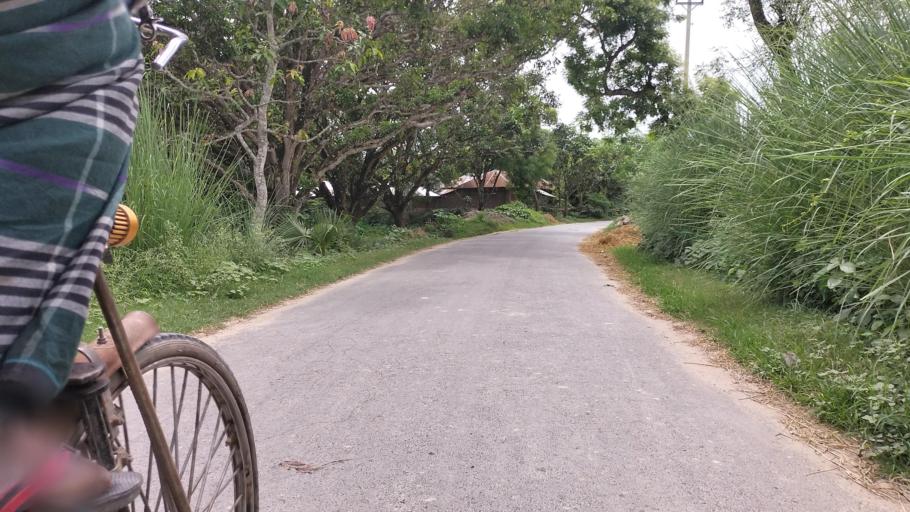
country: BD
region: Rajshahi
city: Rajshahi
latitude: 24.5147
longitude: 88.6300
